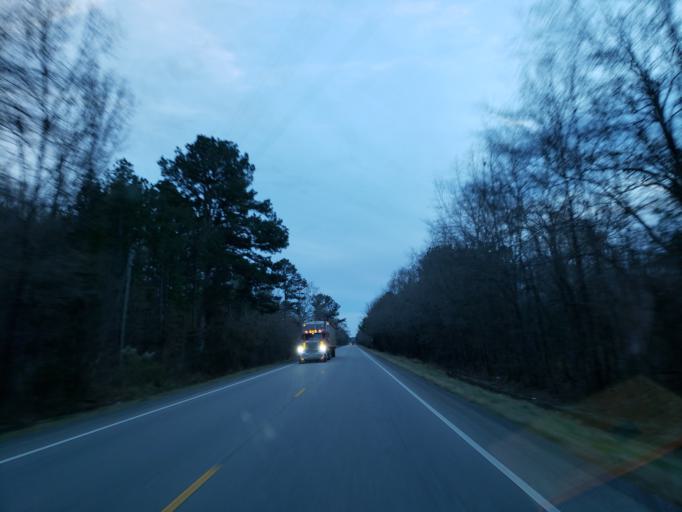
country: US
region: Alabama
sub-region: Sumter County
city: Livingston
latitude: 32.8222
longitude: -88.3103
